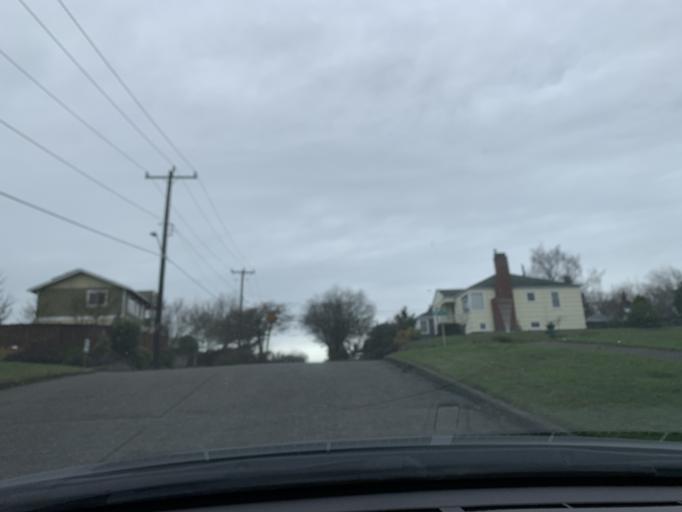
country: US
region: Washington
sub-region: King County
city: White Center
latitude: 47.5557
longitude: -122.3839
